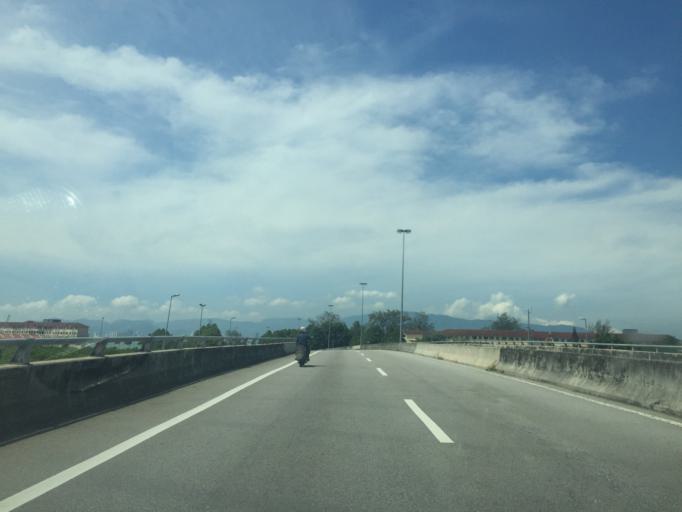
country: MY
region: Penang
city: Permatang Kuching
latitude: 5.4427
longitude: 100.3822
